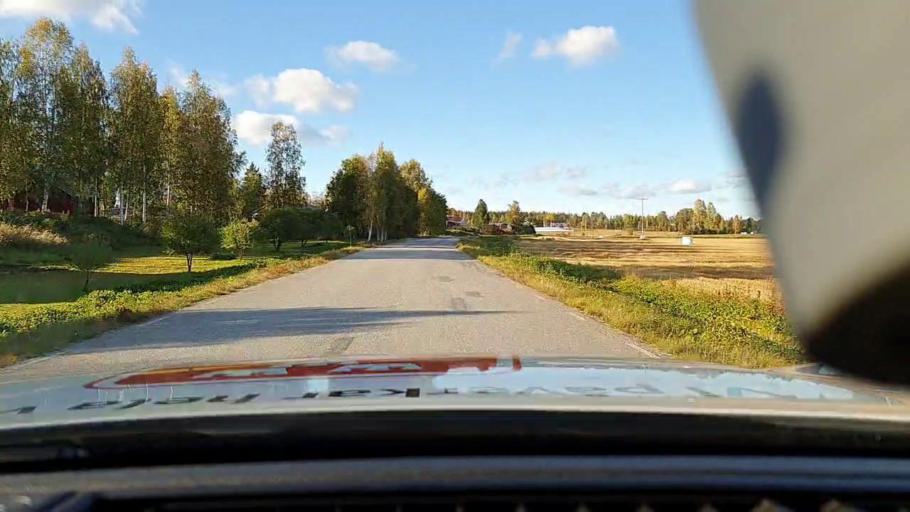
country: SE
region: Norrbotten
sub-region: Pitea Kommun
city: Norrfjarden
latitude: 65.5209
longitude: 21.4938
